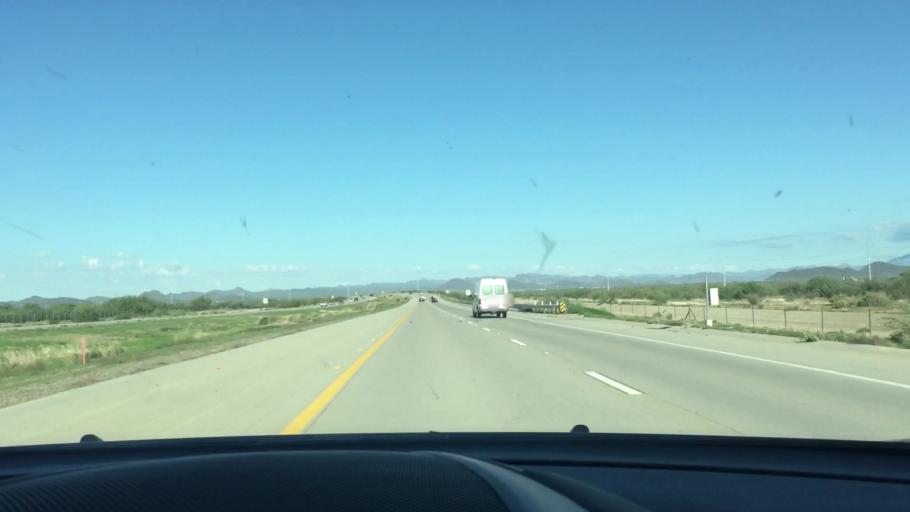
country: US
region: Arizona
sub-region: Maricopa County
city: Anthem
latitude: 33.7771
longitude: -112.1837
